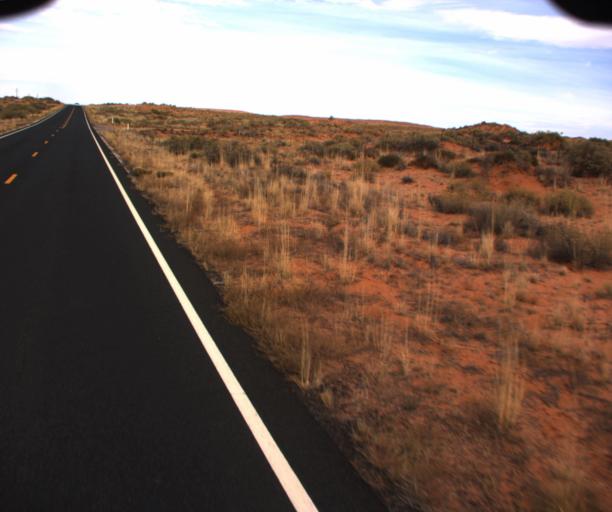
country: US
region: Arizona
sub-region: Apache County
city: Many Farms
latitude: 36.8100
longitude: -109.6472
